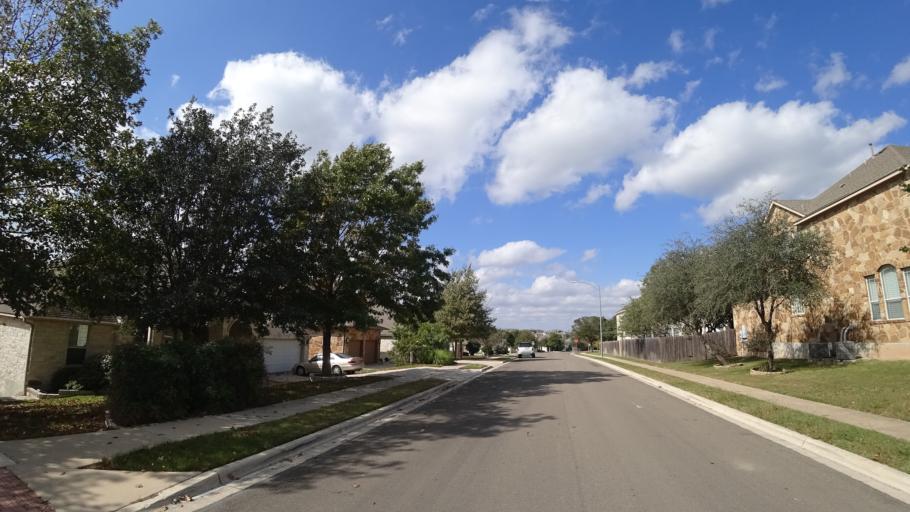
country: US
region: Texas
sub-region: Travis County
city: Barton Creek
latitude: 30.2543
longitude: -97.8860
